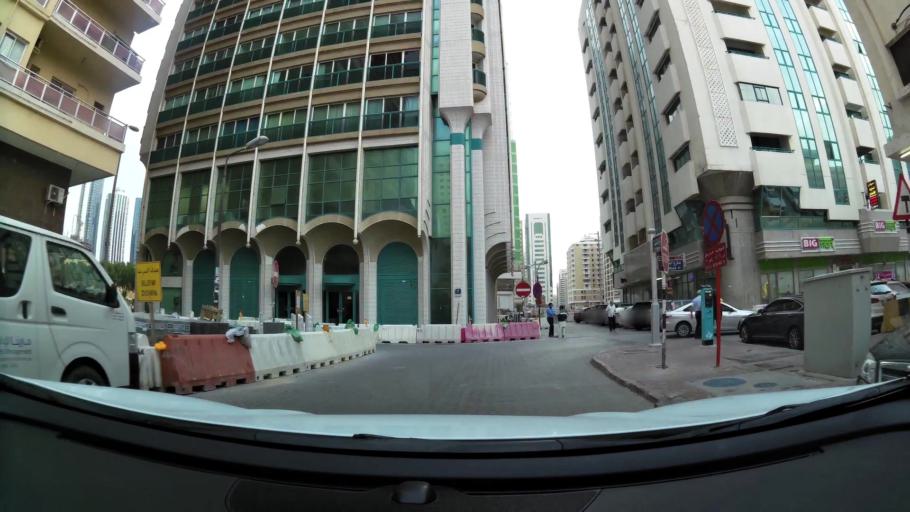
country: AE
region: Abu Dhabi
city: Abu Dhabi
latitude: 24.4986
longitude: 54.3696
